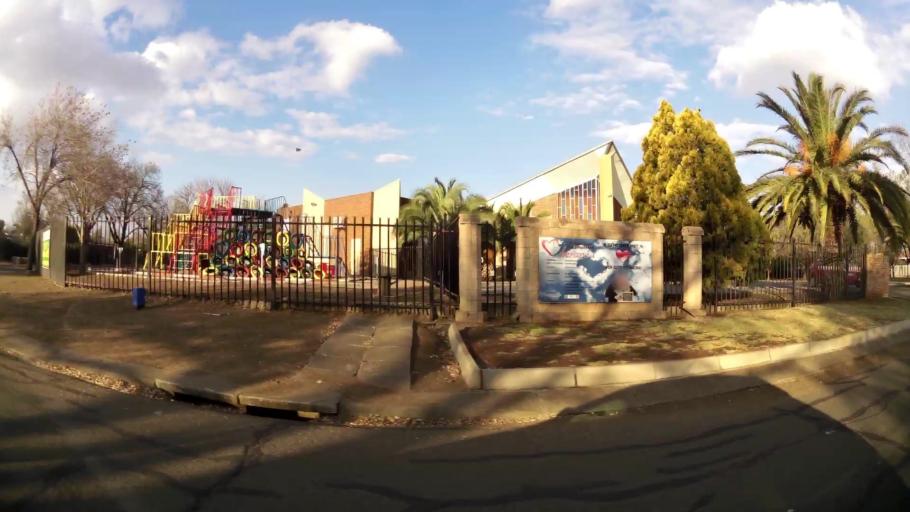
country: ZA
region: Orange Free State
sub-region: Mangaung Metropolitan Municipality
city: Bloemfontein
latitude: -29.1476
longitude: 26.1808
